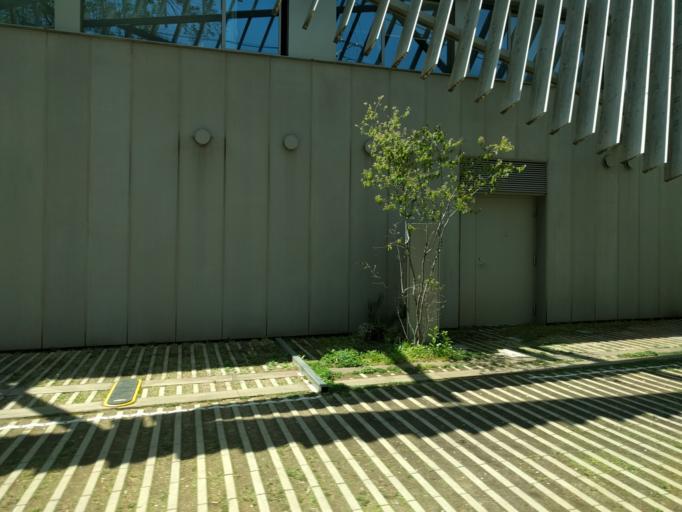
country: JP
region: Tokyo
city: Chofugaoka
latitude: 35.6416
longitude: 139.6002
